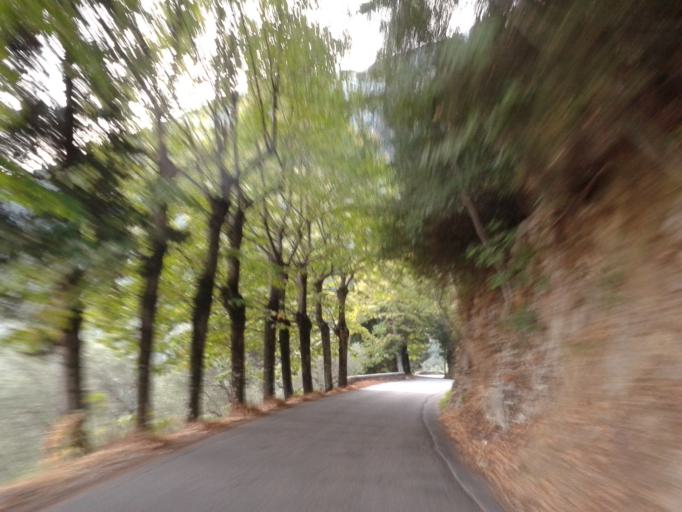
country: IT
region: Tuscany
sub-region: Provincia di Lucca
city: Pontestazzemese
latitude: 43.9543
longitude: 10.3105
